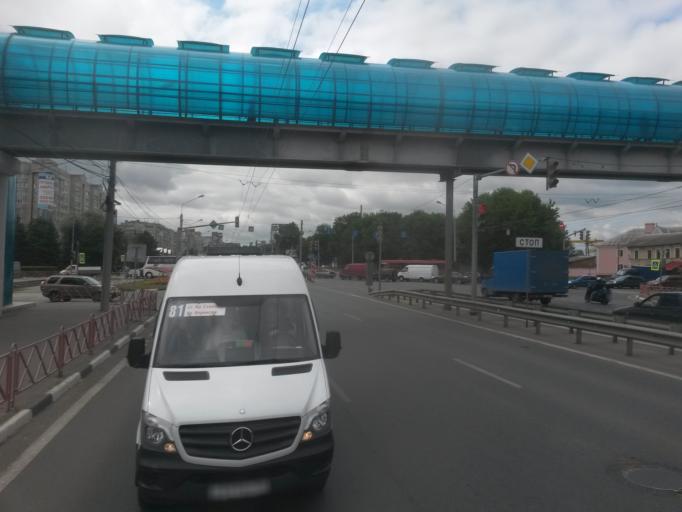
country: RU
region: Jaroslavl
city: Yaroslavl
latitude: 57.5995
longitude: 39.8743
